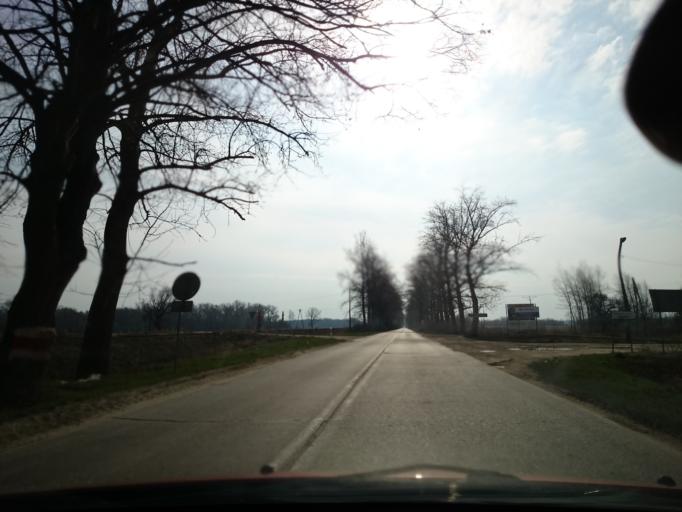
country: PL
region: Opole Voivodeship
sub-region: Powiat nyski
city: Paczkow
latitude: 50.4896
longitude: 16.9736
